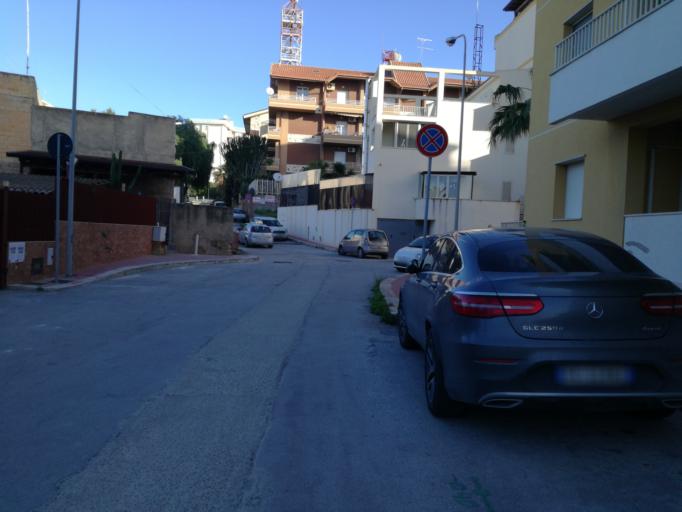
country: IT
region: Sicily
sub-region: Provincia di Caltanissetta
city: Gela
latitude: 37.0737
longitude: 14.2258
